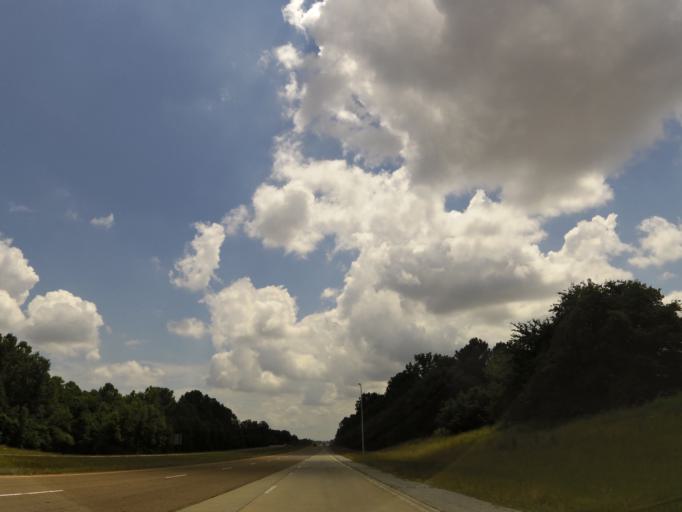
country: US
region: Tennessee
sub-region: Dyer County
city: Dyersburg
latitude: 36.0211
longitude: -89.3409
